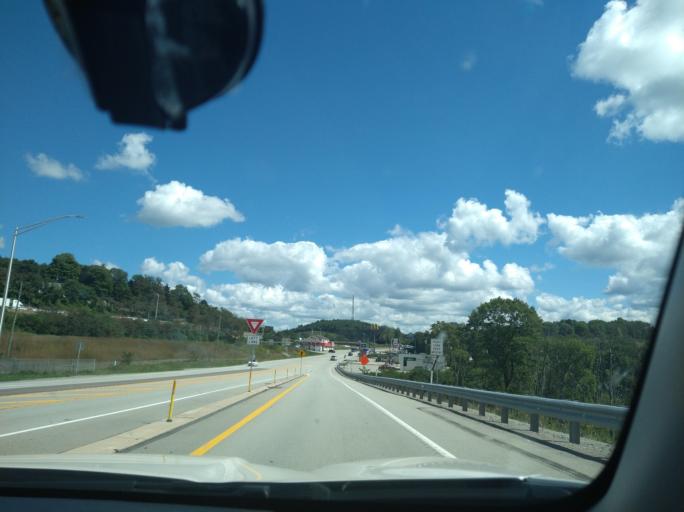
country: US
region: Pennsylvania
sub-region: Fayette County
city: Bear Rocks
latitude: 40.1073
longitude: -79.3816
